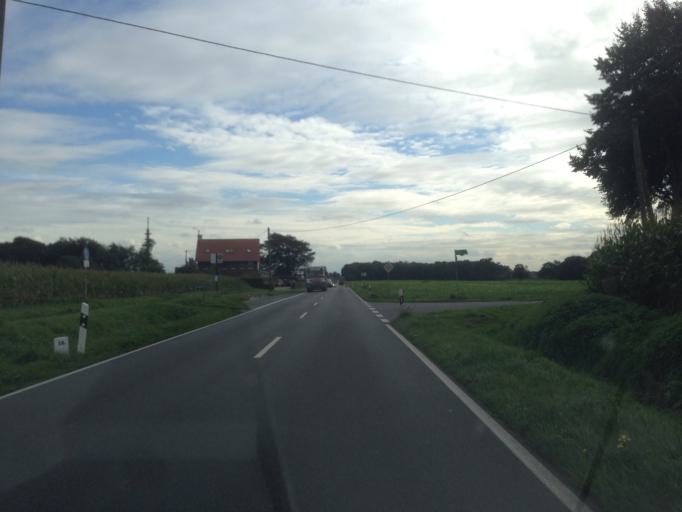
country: DE
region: North Rhine-Westphalia
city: Ludinghausen
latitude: 51.7539
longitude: 7.3995
